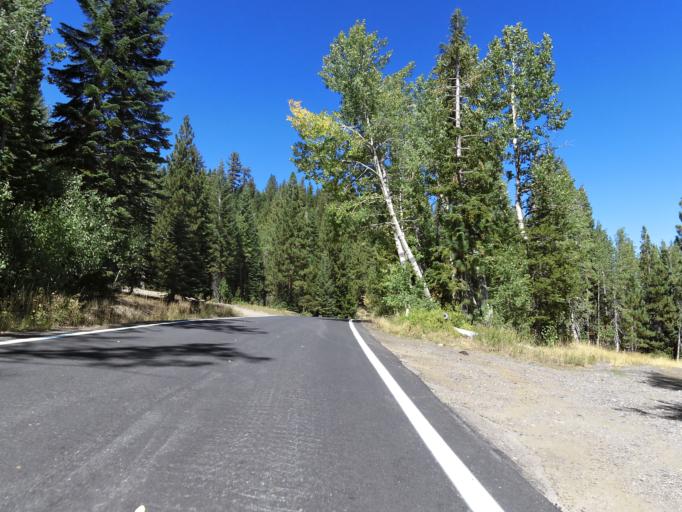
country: US
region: Nevada
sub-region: Douglas County
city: Gardnerville Ranchos
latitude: 38.5782
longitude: -119.8070
